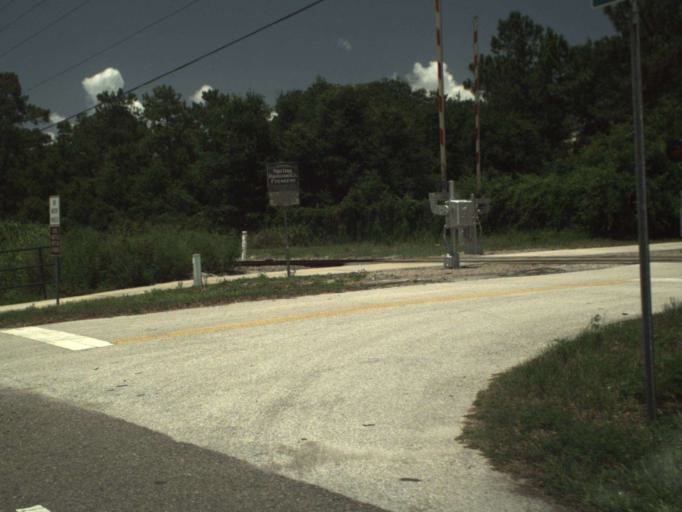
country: US
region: Florida
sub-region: Seminole County
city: Winter Springs
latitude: 28.7216
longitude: -81.3094
